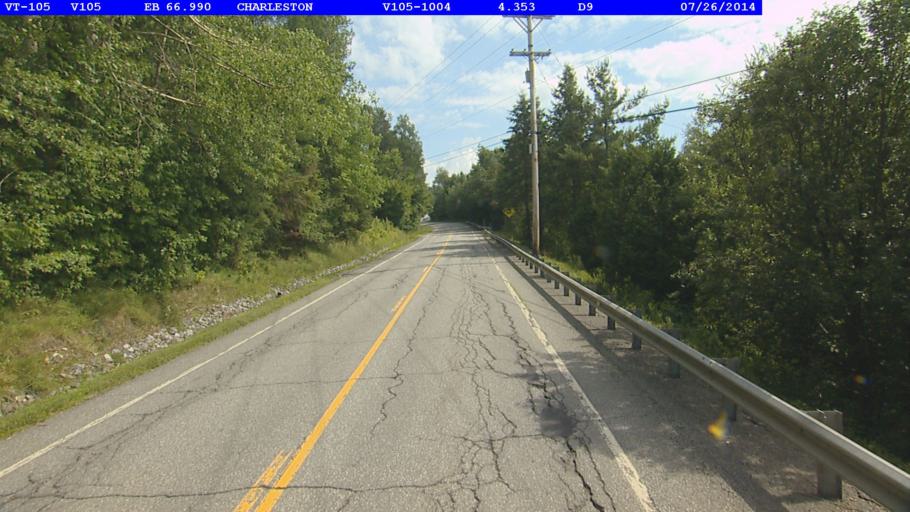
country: US
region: Vermont
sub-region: Orleans County
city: Newport
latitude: 44.8580
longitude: -72.0350
